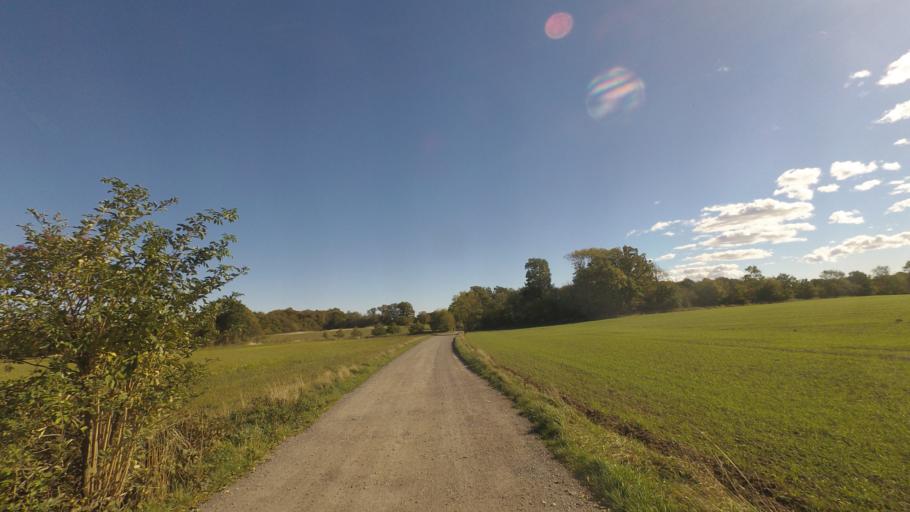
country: DK
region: Capital Region
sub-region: Bornholm Kommune
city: Nexo
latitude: 55.1207
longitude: 15.0565
